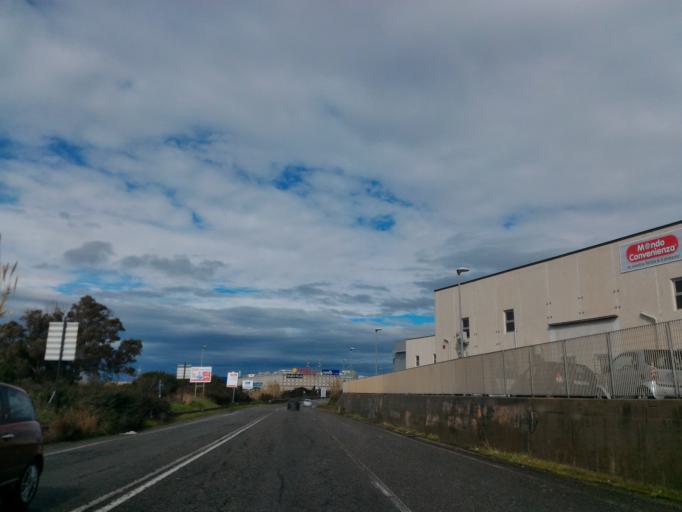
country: IT
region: Latium
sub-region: Citta metropolitana di Roma Capitale
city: Aurelia
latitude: 42.1215
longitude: 11.7705
